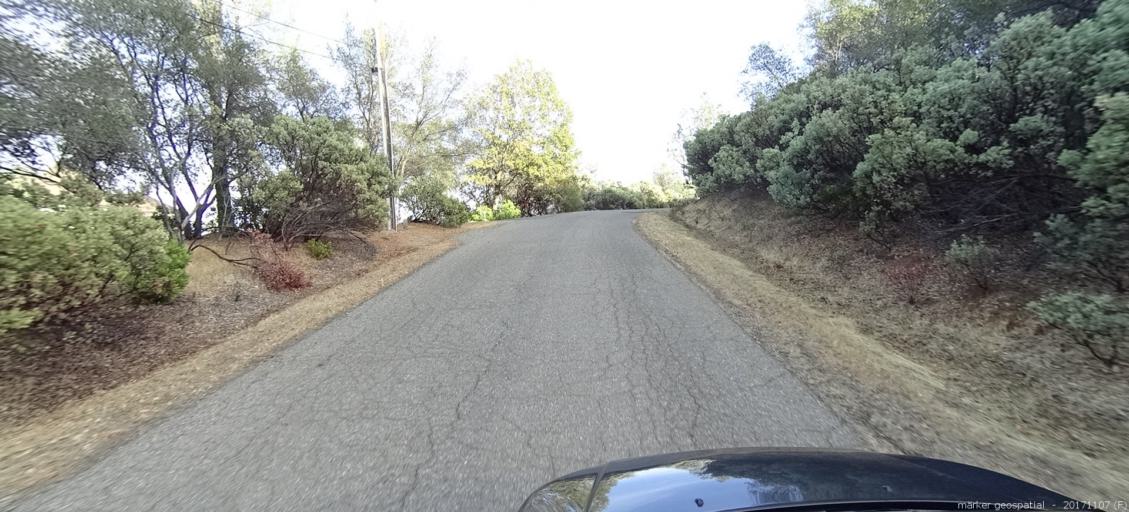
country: US
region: California
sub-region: Shasta County
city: Shasta
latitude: 40.5344
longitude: -122.4876
